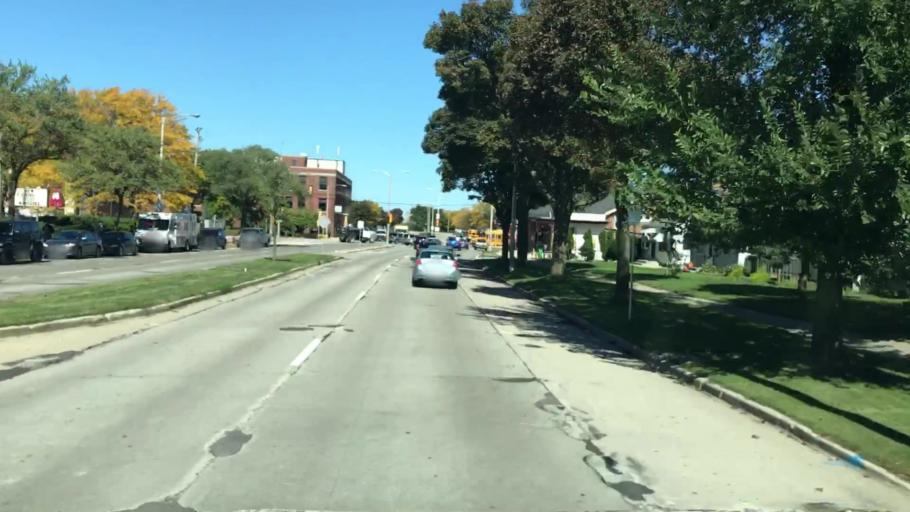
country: US
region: Wisconsin
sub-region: Milwaukee County
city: Saint Francis
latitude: 42.9870
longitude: -87.9094
